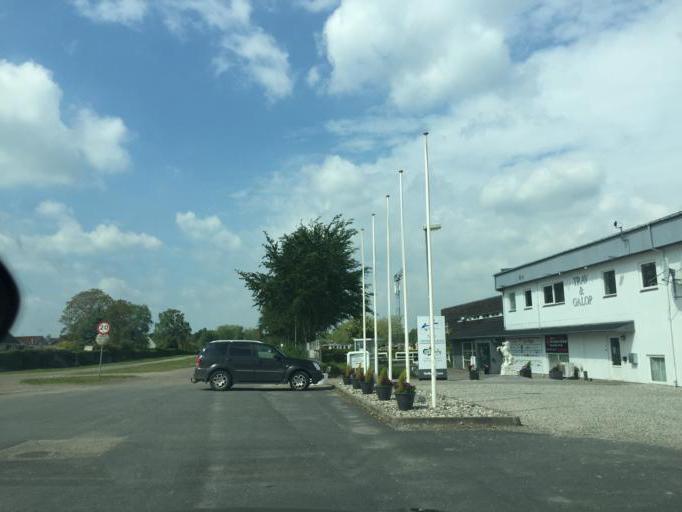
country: DK
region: South Denmark
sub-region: Odense Kommune
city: Odense
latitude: 55.3744
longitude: 10.3520
